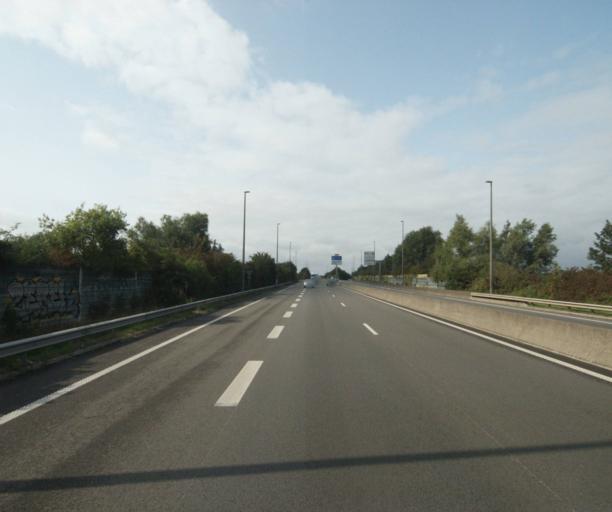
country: FR
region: Nord-Pas-de-Calais
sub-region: Departement du Nord
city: Saint-Andre-lez-Lille
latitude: 50.6691
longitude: 3.0338
